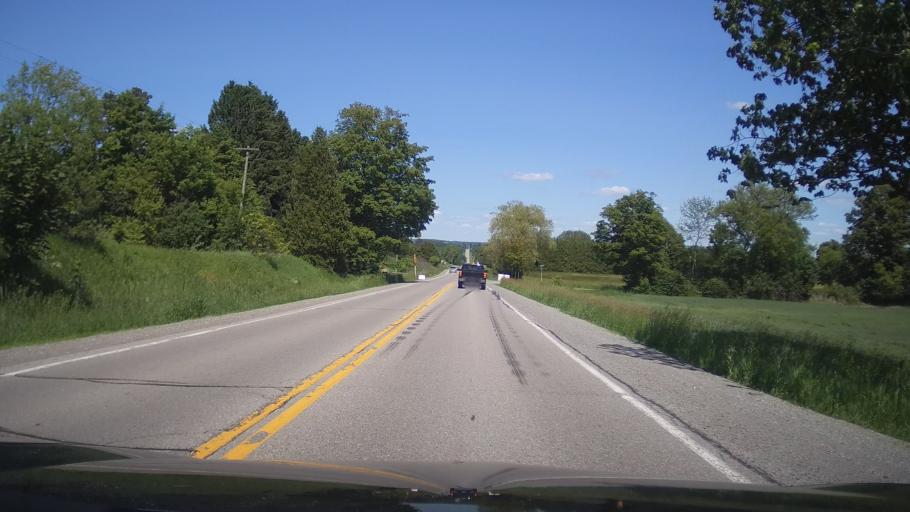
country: CA
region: Ontario
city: Oshawa
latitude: 44.0082
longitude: -78.8003
